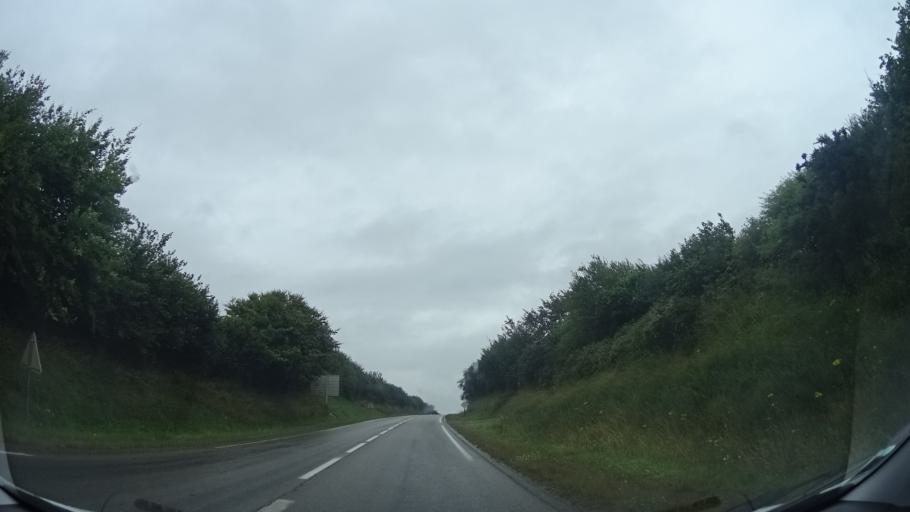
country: FR
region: Lower Normandy
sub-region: Departement de la Manche
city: Urville-Nacqueville
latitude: 49.6048
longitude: -1.7342
